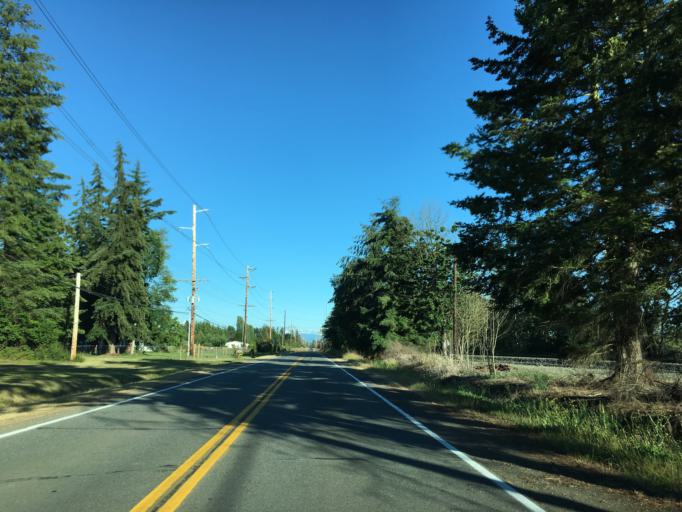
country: US
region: Washington
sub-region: Whatcom County
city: Birch Bay
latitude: 48.9299
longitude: -122.6595
